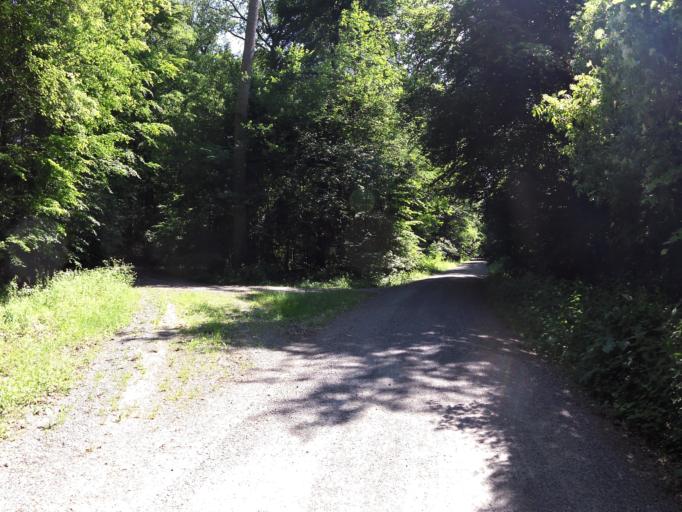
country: DE
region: Bavaria
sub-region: Regierungsbezirk Unterfranken
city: Kleinrinderfeld
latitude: 49.7154
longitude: 9.8616
